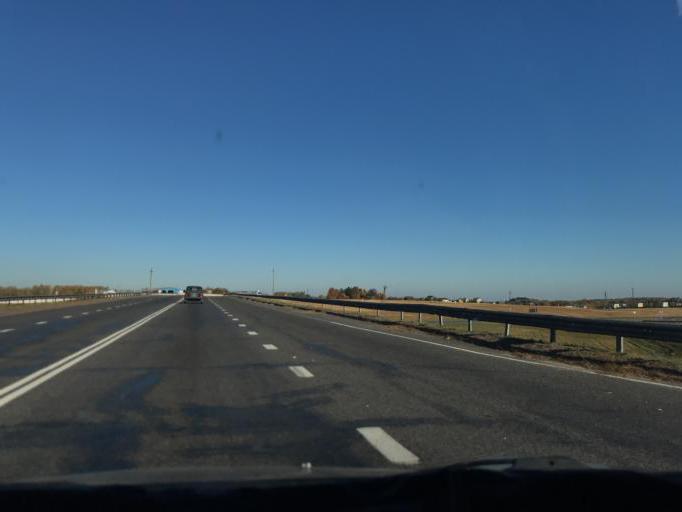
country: BY
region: Gomel
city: Mazyr
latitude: 52.0145
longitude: 29.2704
